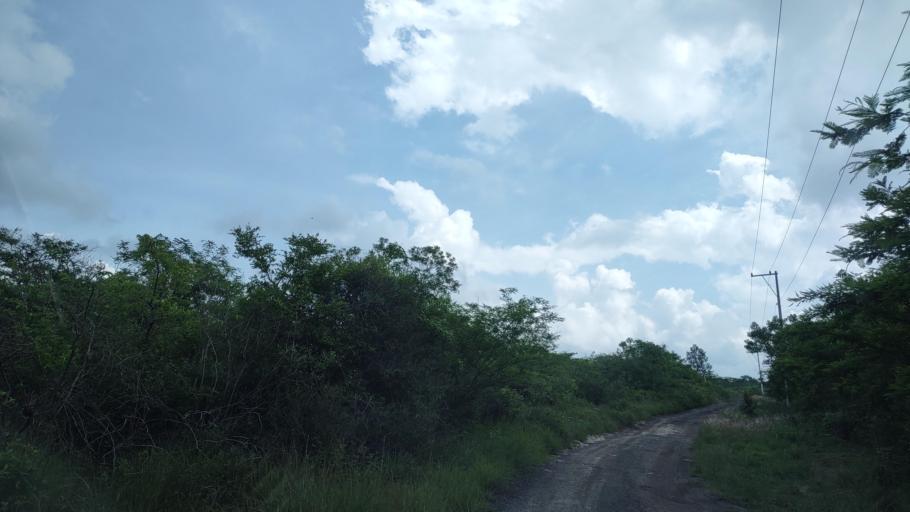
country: MX
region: Veracruz
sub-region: Emiliano Zapata
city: Dos Rios
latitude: 19.4510
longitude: -96.8092
